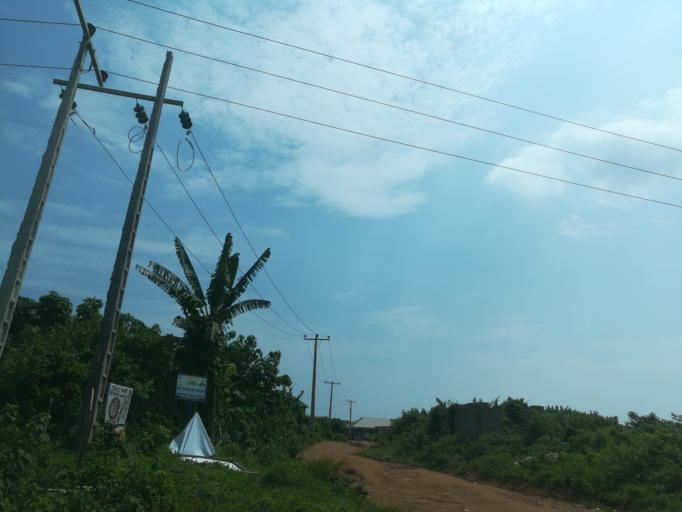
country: NG
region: Lagos
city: Ikorodu
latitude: 6.5941
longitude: 3.6373
